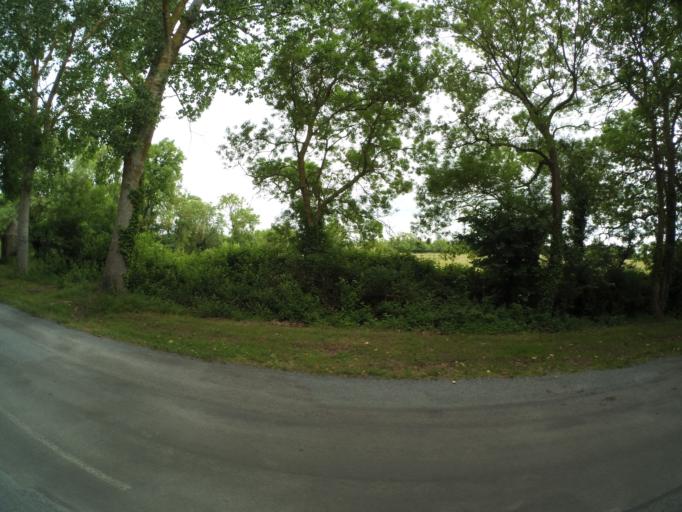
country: FR
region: Poitou-Charentes
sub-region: Departement de la Charente-Maritime
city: Saint-Laurent-de-la-Pree
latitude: 45.9831
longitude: -1.0052
